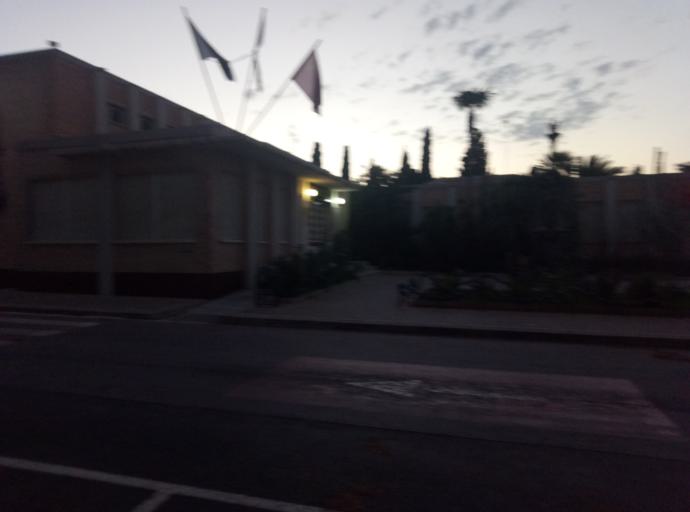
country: ES
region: Murcia
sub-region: Murcia
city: Cartagena
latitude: 37.6378
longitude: -1.0121
